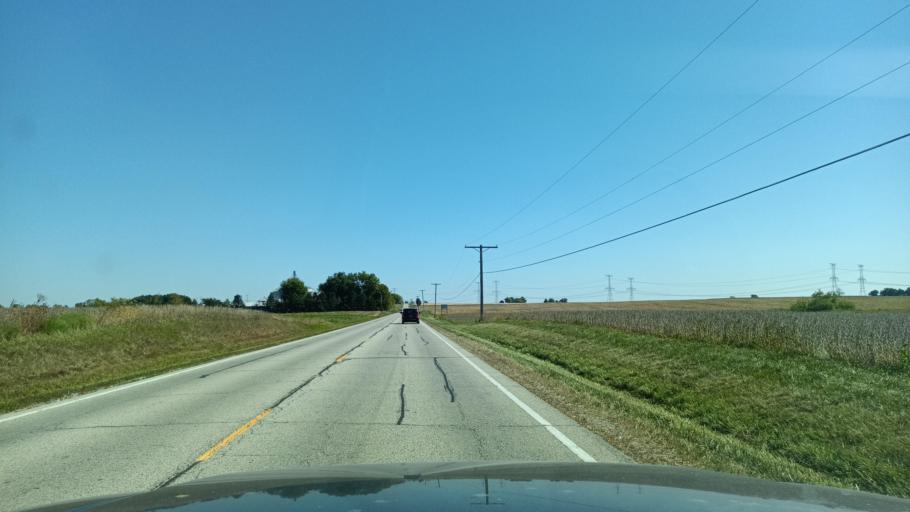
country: US
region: Illinois
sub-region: Tazewell County
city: Morton
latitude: 40.6135
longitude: -89.4245
